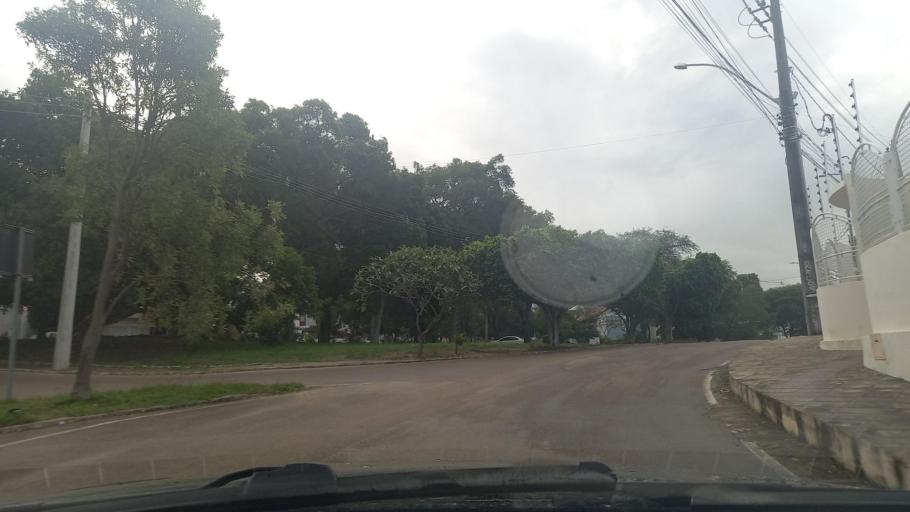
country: BR
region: Bahia
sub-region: Paulo Afonso
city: Paulo Afonso
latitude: -9.3968
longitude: -38.2143
